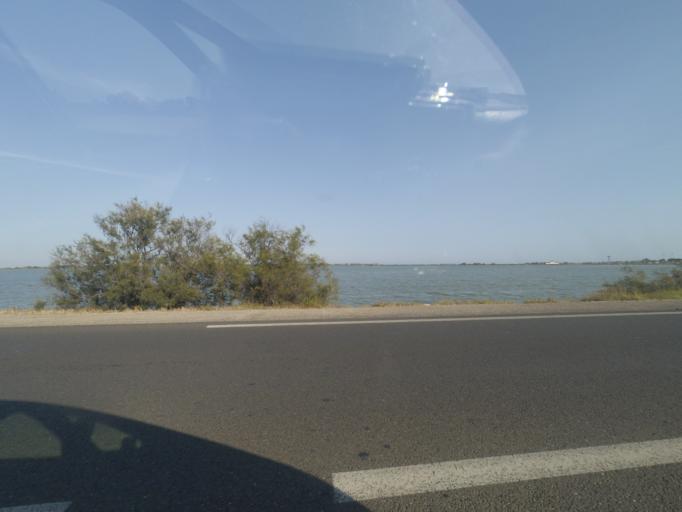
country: FR
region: Languedoc-Roussillon
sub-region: Departement du Gard
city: Le Grau-du-Roi
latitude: 43.5483
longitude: 4.1404
